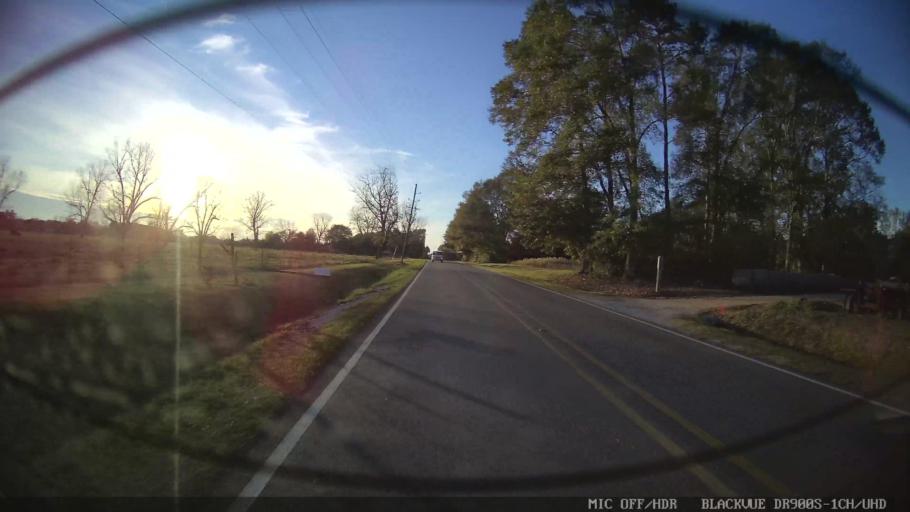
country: US
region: Mississippi
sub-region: Lamar County
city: Lumberton
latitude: 30.9972
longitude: -89.3946
